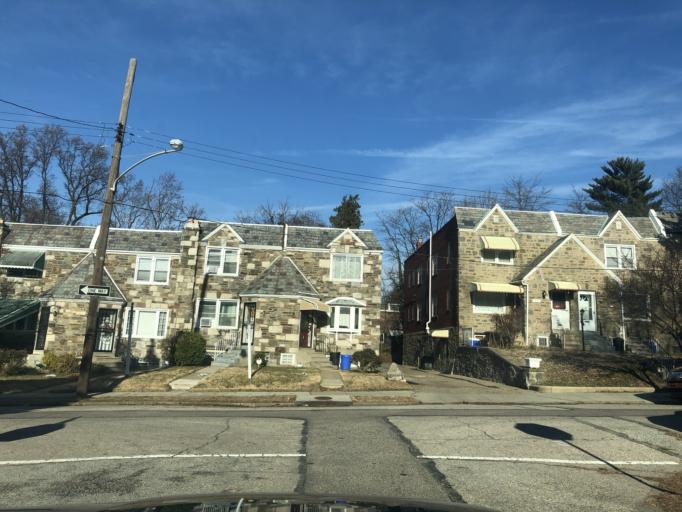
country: US
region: Pennsylvania
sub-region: Montgomery County
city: Bala-Cynwyd
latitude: 39.9862
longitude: -75.2438
